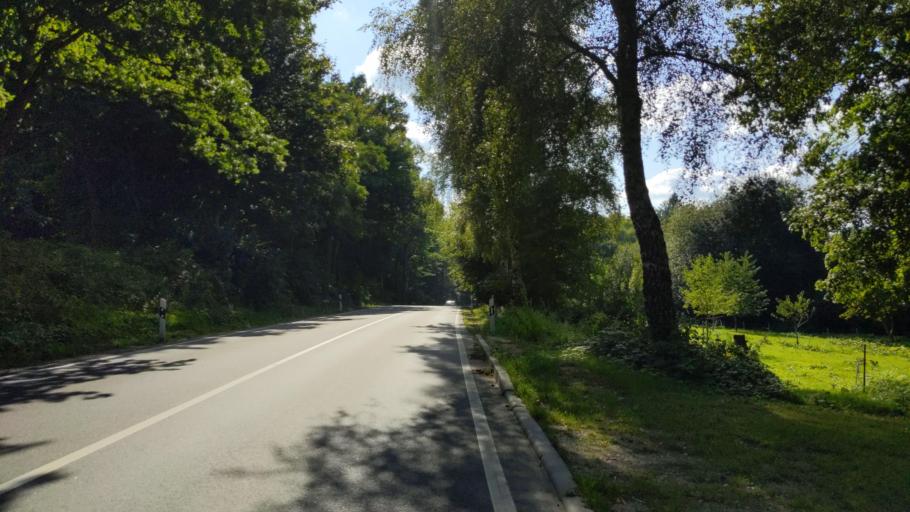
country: DE
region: Schleswig-Holstein
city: Kasseedorf
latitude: 54.1557
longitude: 10.7194
